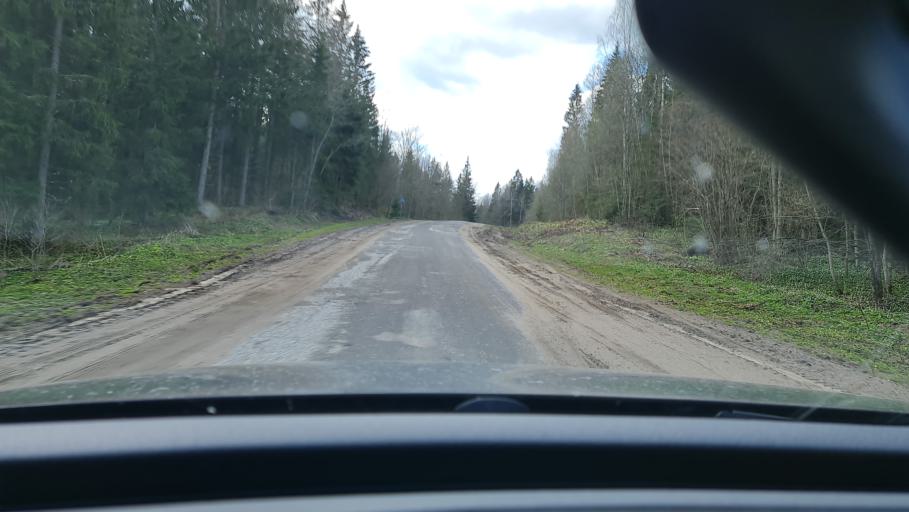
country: RU
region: Tverskaya
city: Toropets
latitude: 56.6247
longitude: 31.4314
